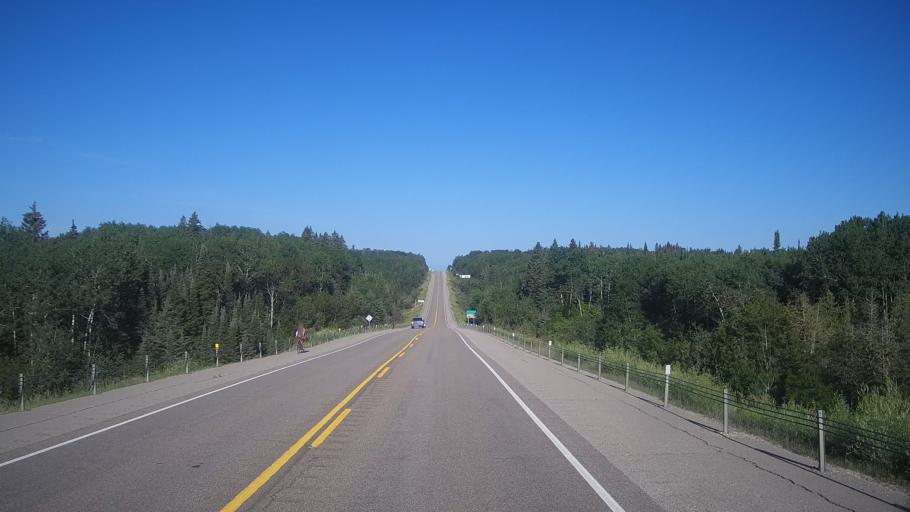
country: US
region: Minnesota
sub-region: Roseau County
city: Warroad
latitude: 49.7373
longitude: -95.1914
